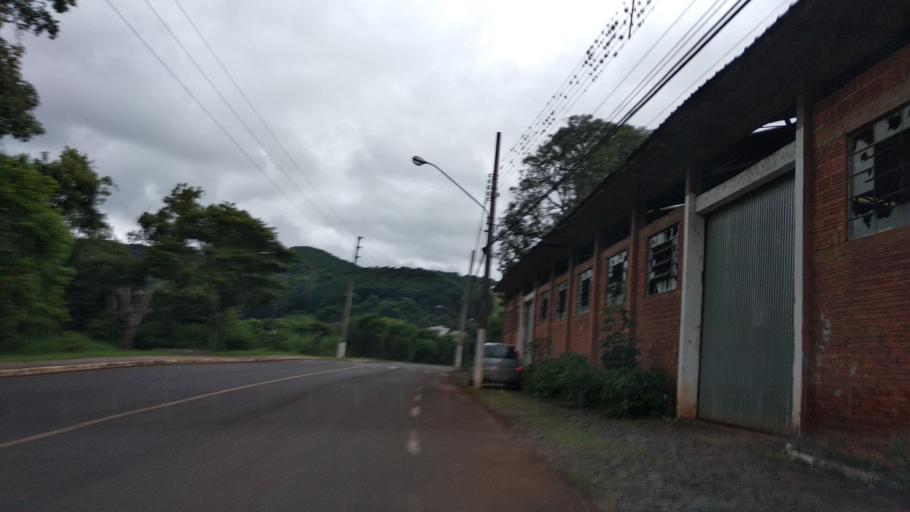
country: BR
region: Santa Catarina
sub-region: Videira
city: Videira
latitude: -27.0506
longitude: -51.2320
